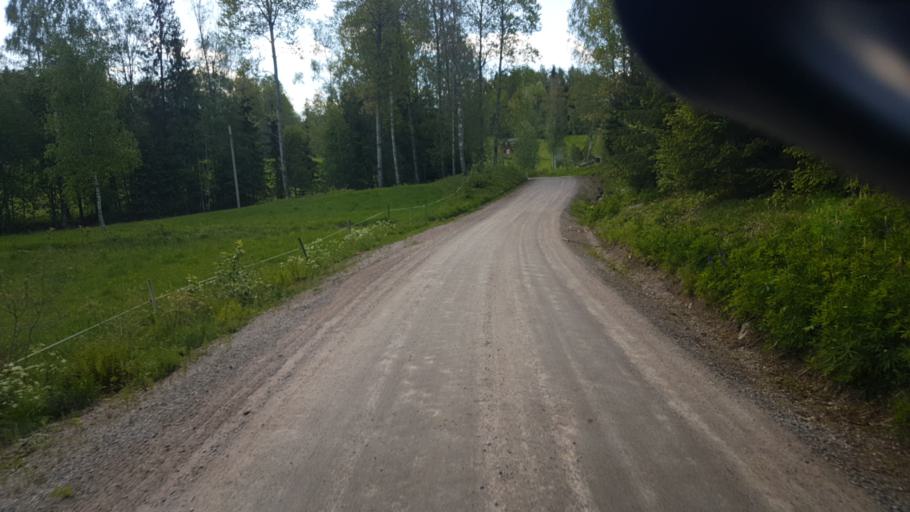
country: SE
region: Vaermland
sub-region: Arvika Kommun
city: Arvika
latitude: 59.6787
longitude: 12.7690
